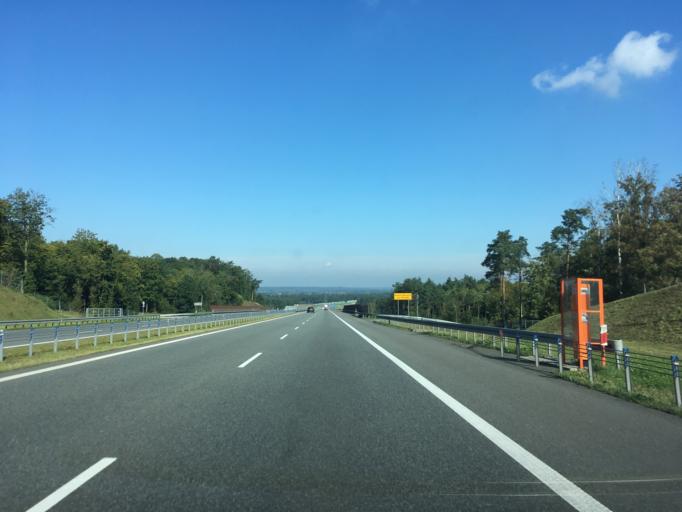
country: PL
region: Kujawsko-Pomorskie
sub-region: Powiat chelminski
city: Lisewo
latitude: 53.3898
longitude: 18.6861
